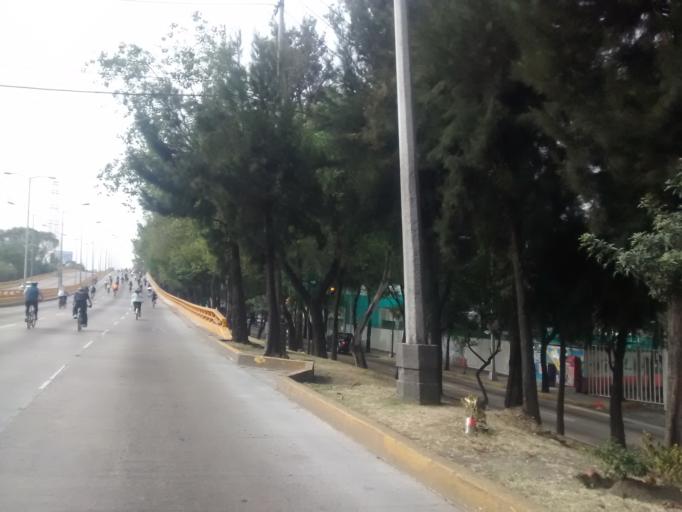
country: MX
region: Mexico City
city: Colonia Nativitas
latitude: 19.3628
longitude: -99.1288
